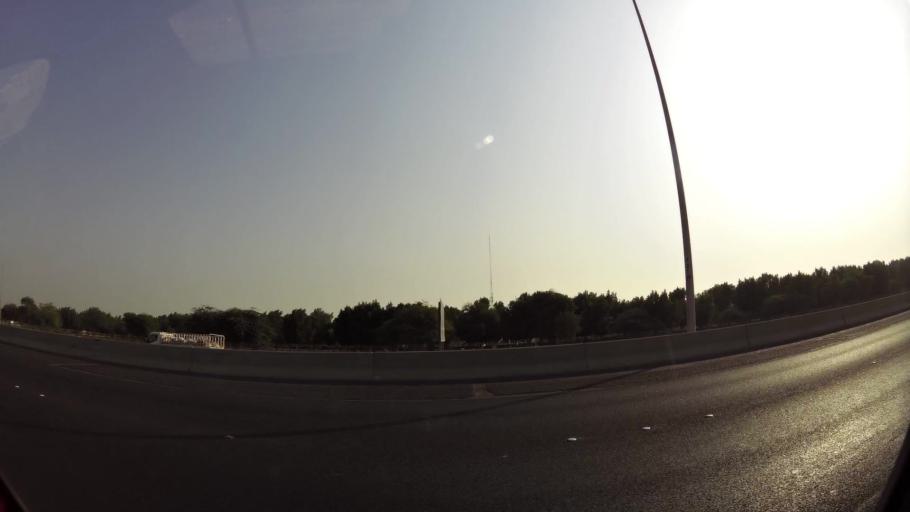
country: KW
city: Al Funaytis
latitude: 29.2448
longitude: 48.0929
